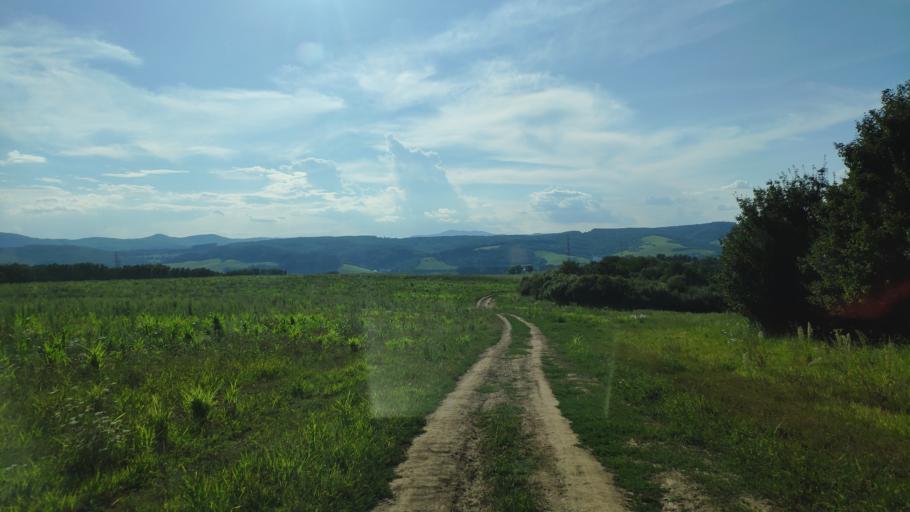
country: SK
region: Presovsky
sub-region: Okres Presov
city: Presov
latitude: 48.9129
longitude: 21.2770
